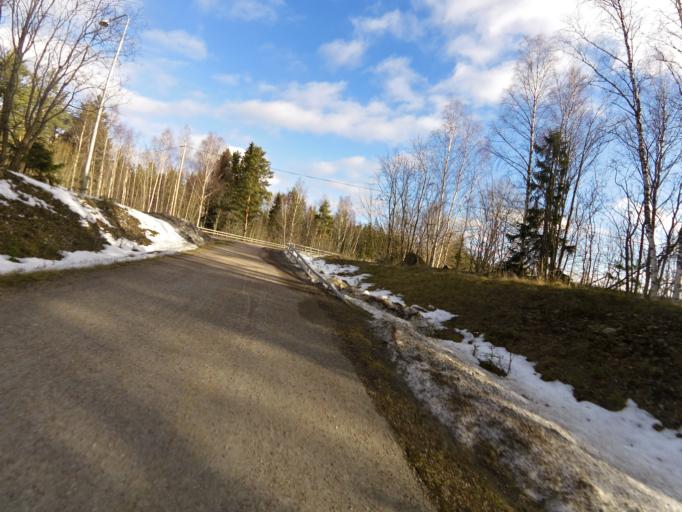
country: SE
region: Uppsala
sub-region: Alvkarleby Kommun
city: Skutskaer
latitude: 60.6502
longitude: 17.3172
